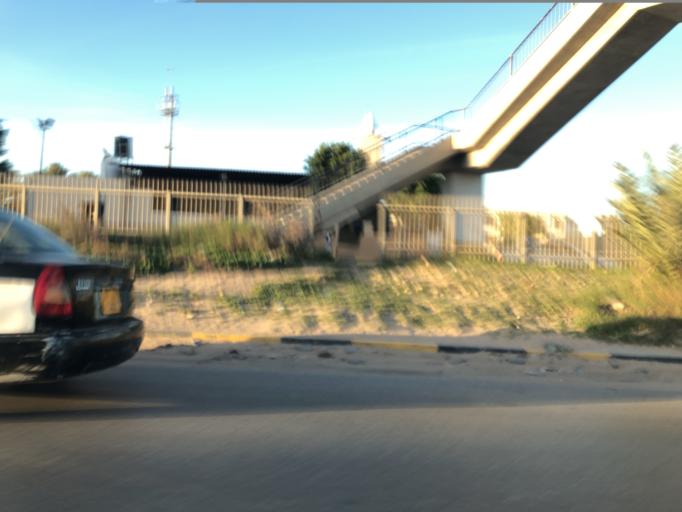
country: LY
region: Tripoli
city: Tagiura
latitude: 32.8690
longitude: 13.2915
